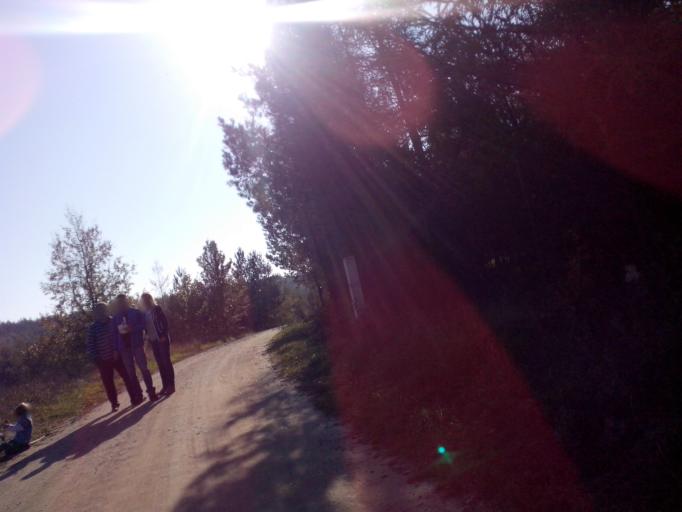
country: PL
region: Kujawsko-Pomorskie
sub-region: Powiat brodnicki
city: Gorzno
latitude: 53.2001
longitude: 19.6586
